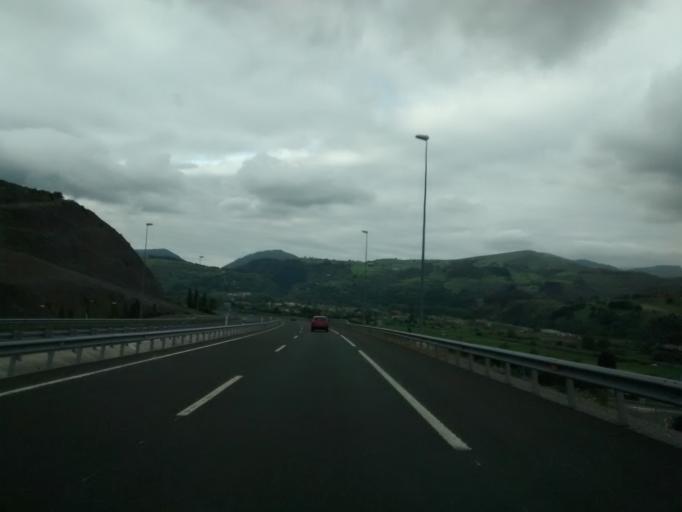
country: ES
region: Cantabria
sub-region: Provincia de Cantabria
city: Arenas de Iguna
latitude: 43.1653
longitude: -4.0525
